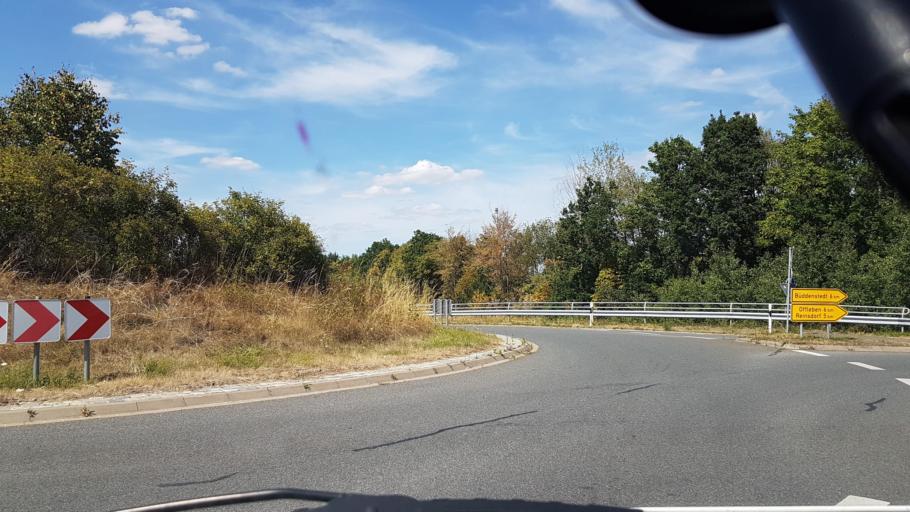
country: DE
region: Lower Saxony
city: Schoningen
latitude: 52.1495
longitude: 10.9734
